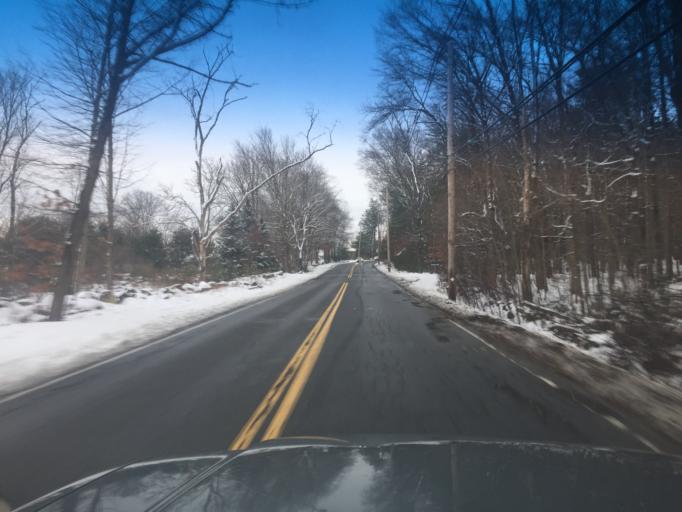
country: US
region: Massachusetts
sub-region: Middlesex County
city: Holliston
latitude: 42.1938
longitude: -71.4174
